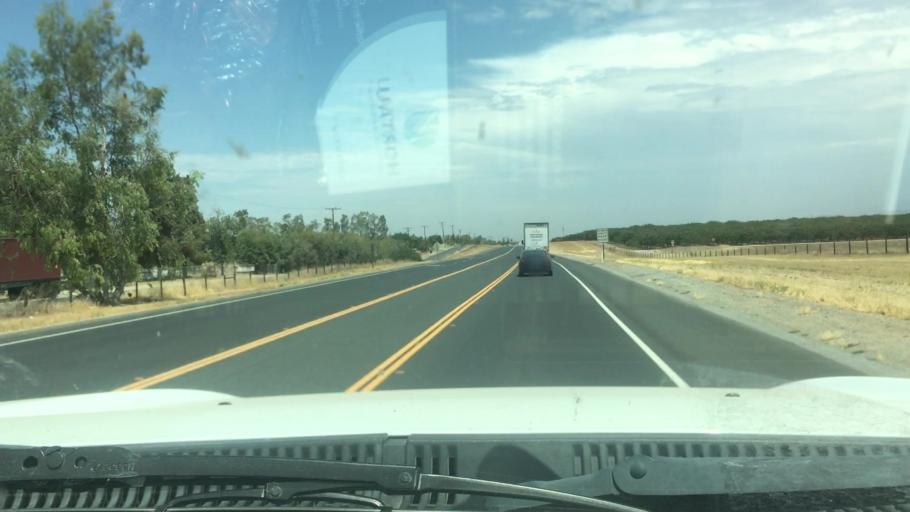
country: US
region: California
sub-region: Tulare County
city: Terra Bella
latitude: 35.9110
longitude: -119.0535
